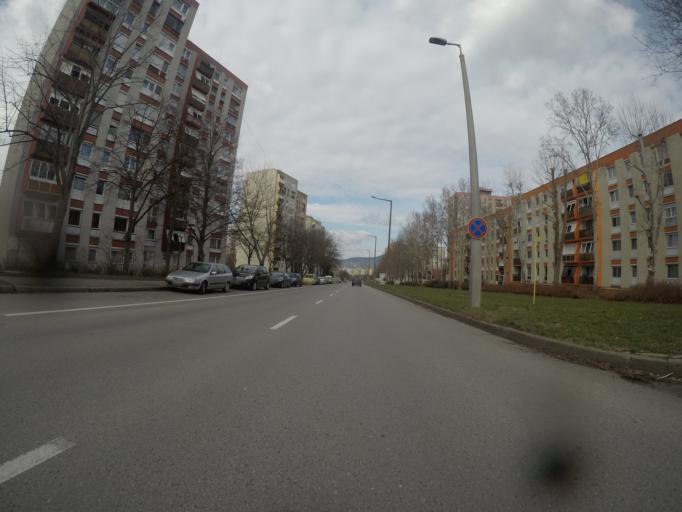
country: HU
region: Baranya
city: Pecs
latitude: 46.0405
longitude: 18.2279
